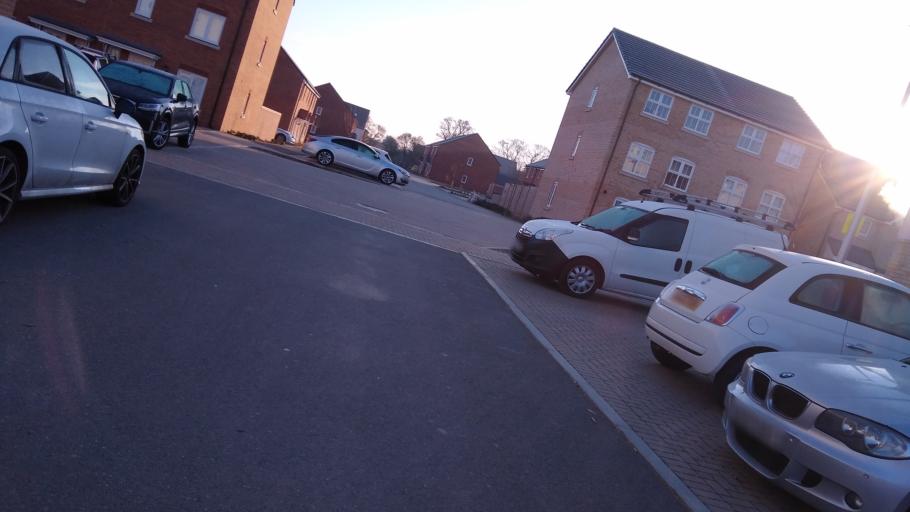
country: GB
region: England
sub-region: Wokingham
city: Winnersh
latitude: 51.4277
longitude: -0.8890
